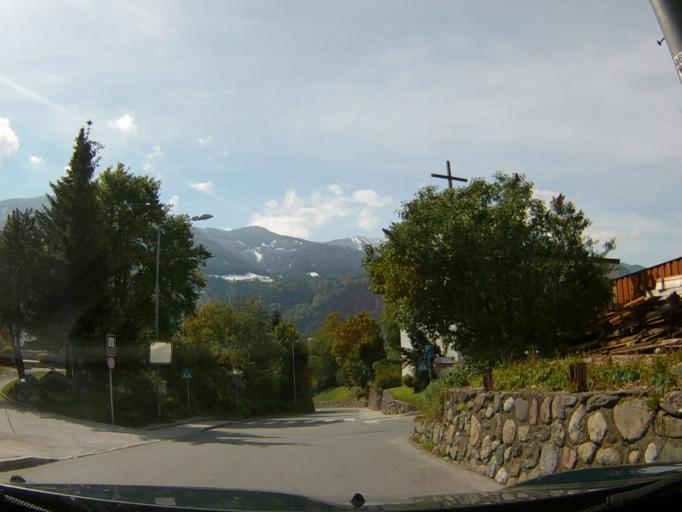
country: AT
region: Tyrol
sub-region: Politischer Bezirk Schwaz
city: Jenbach
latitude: 47.3941
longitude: 11.7714
